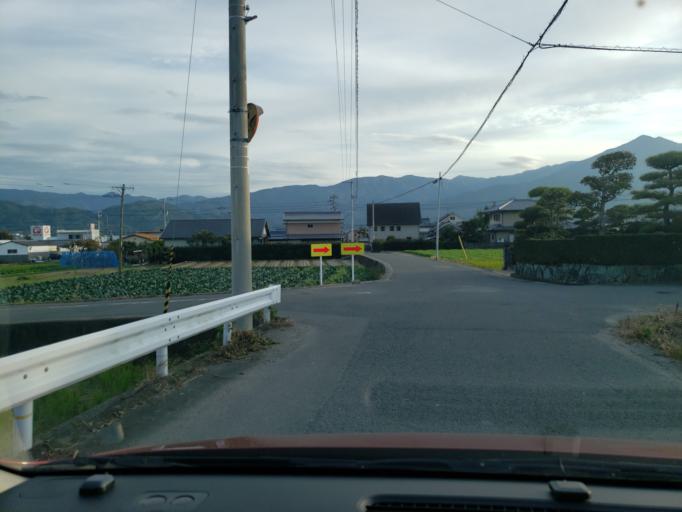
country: JP
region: Tokushima
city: Wakimachi
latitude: 34.0758
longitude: 134.2277
